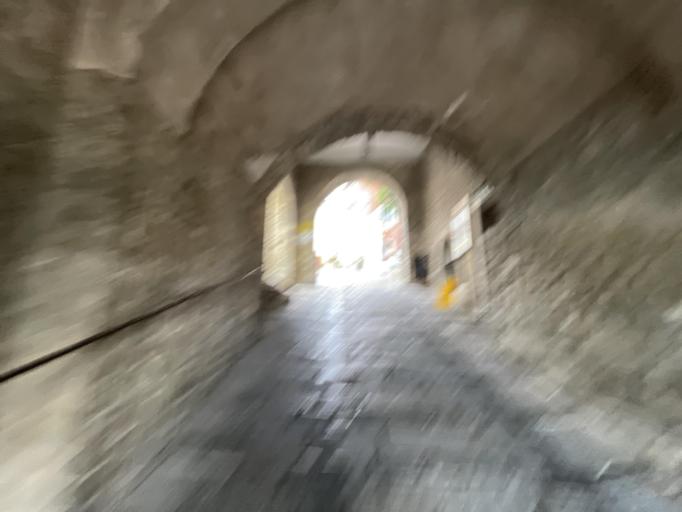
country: HR
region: Istarska
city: Karojba
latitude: 45.3367
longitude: 13.8281
